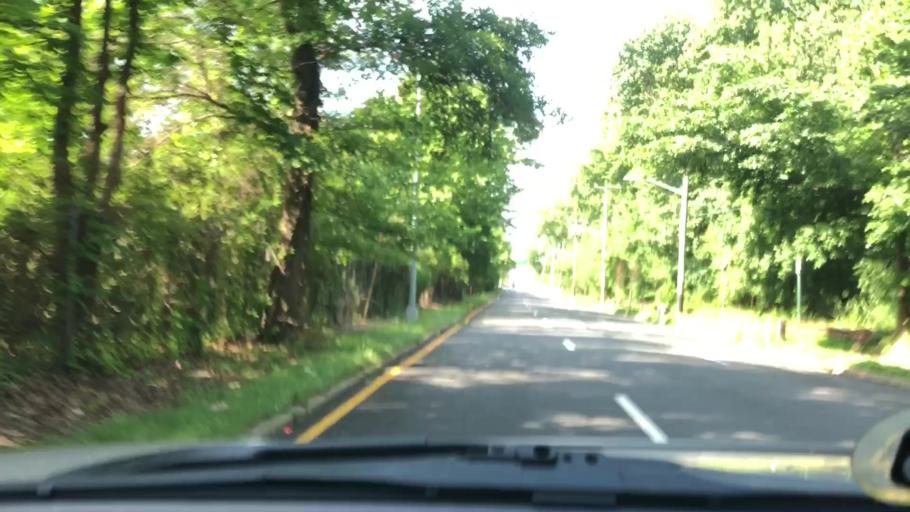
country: US
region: New York
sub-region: Richmond County
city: Staten Island
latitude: 40.5436
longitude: -74.1842
